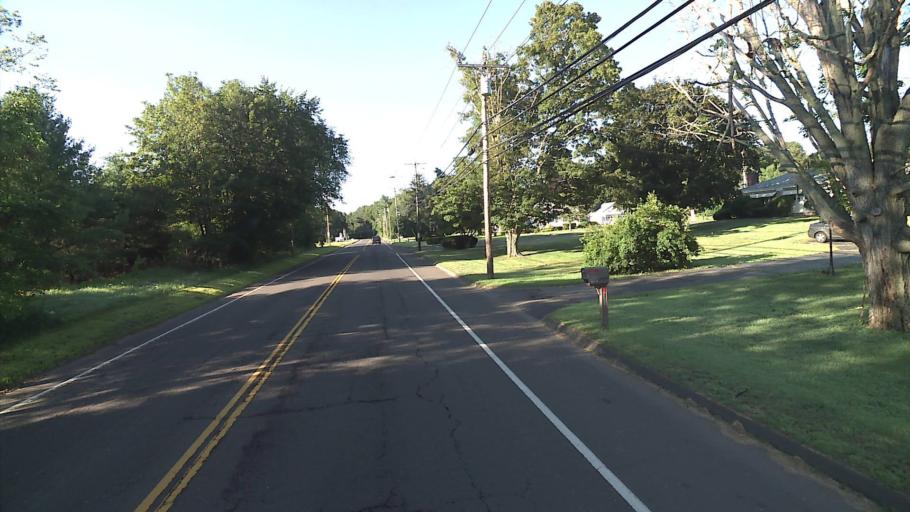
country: US
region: Connecticut
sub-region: New Haven County
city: Hamden
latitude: 41.4447
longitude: -72.9106
